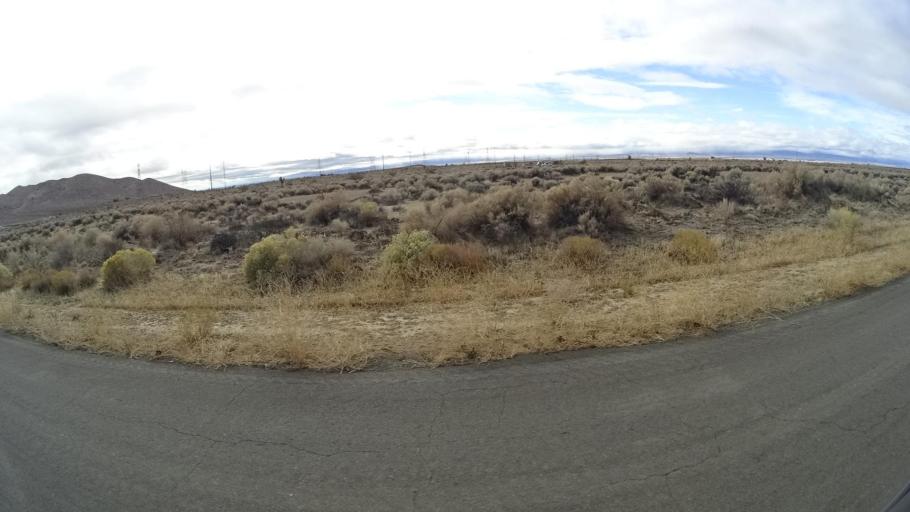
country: US
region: California
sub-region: Kern County
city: Rosamond
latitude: 34.8927
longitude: -118.3020
